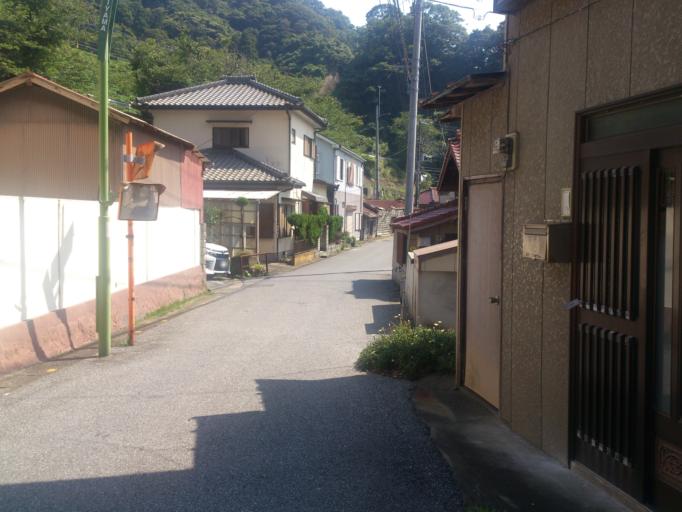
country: JP
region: Chiba
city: Tateyama
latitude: 35.0787
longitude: 139.8392
